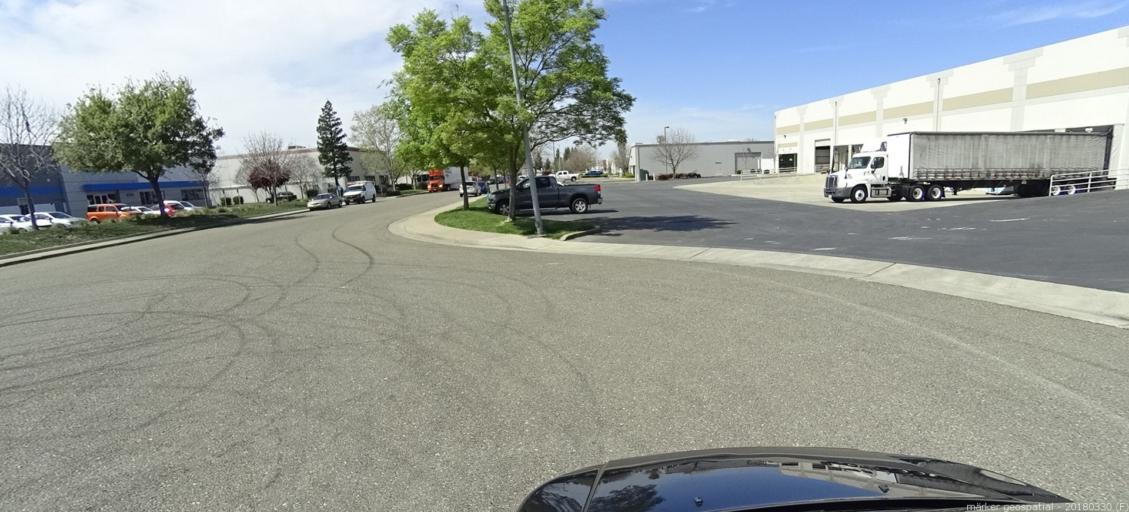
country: US
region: California
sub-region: Sacramento County
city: Rosemont
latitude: 38.5390
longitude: -121.3537
